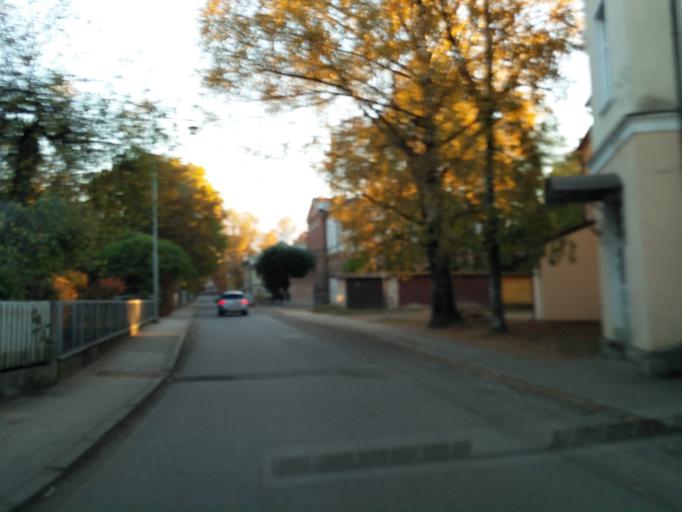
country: EE
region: Tartu
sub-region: Tartu linn
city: Tartu
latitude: 58.3820
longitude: 26.7095
